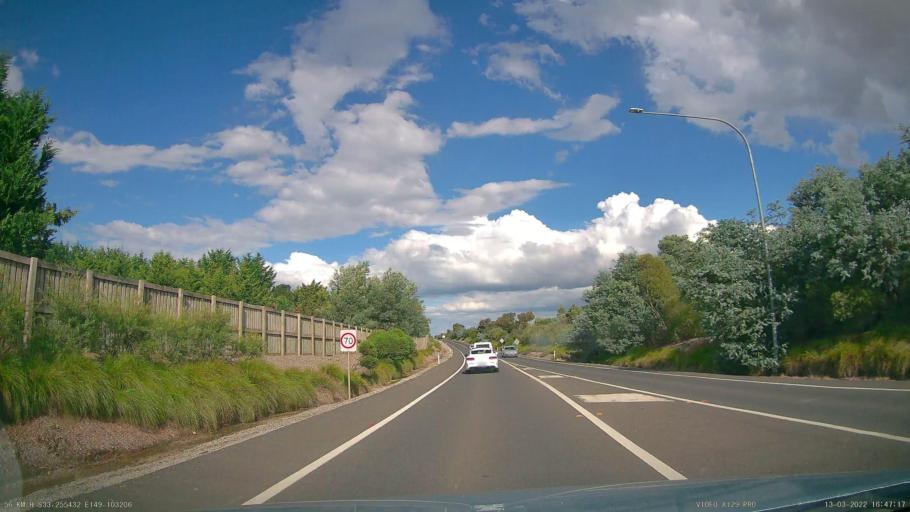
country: AU
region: New South Wales
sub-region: Orange Municipality
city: Orange
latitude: -33.2552
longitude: 149.1028
